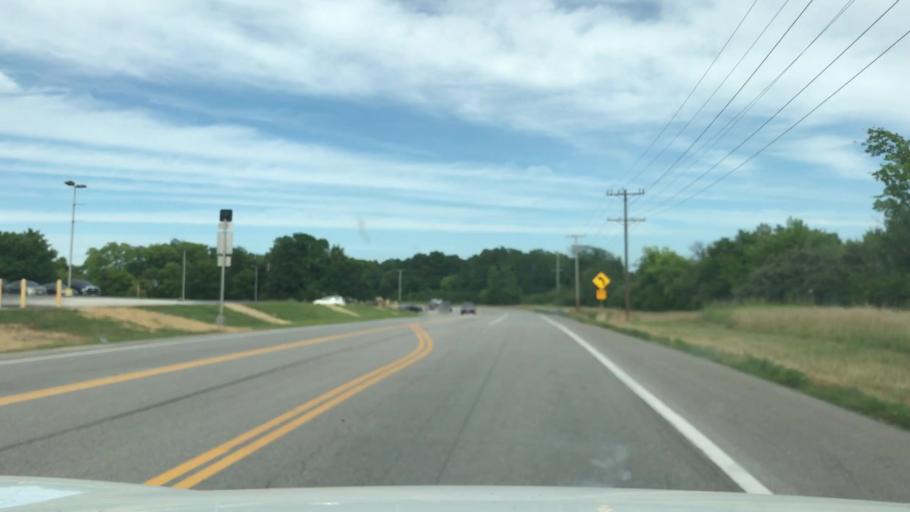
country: US
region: Missouri
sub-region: Saint Charles County
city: Weldon Spring
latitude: 38.7011
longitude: -90.7155
